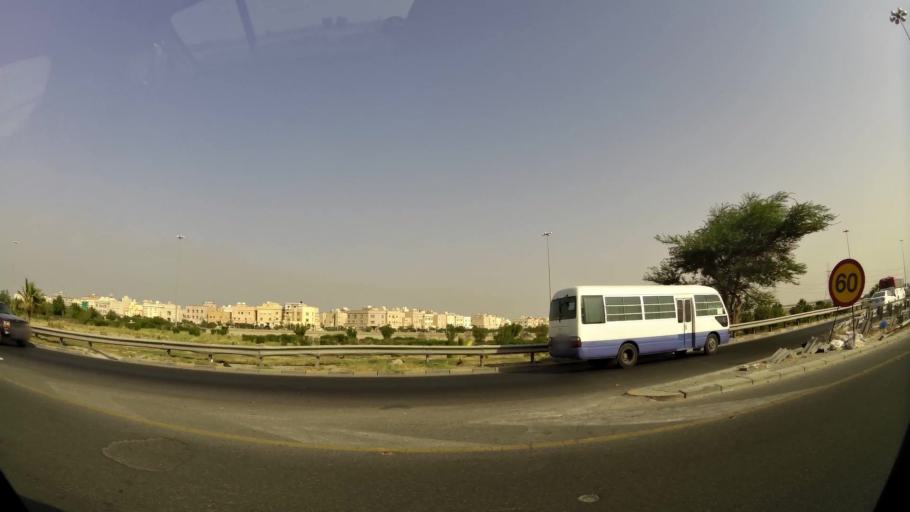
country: KW
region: Muhafazat al Jahra'
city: Al Jahra'
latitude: 29.3034
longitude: 47.7837
